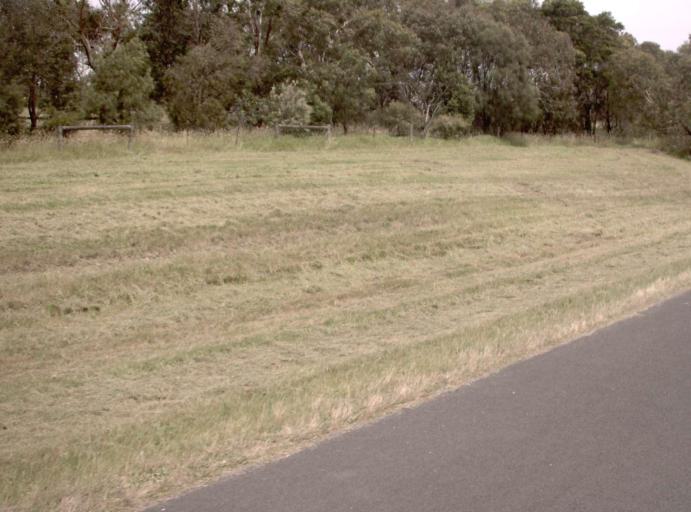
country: AU
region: Victoria
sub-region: Mornington Peninsula
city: Safety Beach
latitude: -38.3104
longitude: 145.0188
